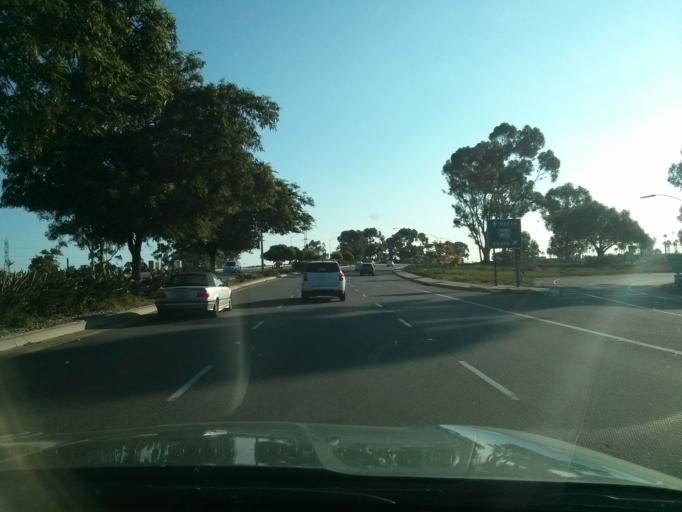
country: US
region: California
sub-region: San Diego County
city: San Diego
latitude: 32.8210
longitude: -117.1653
